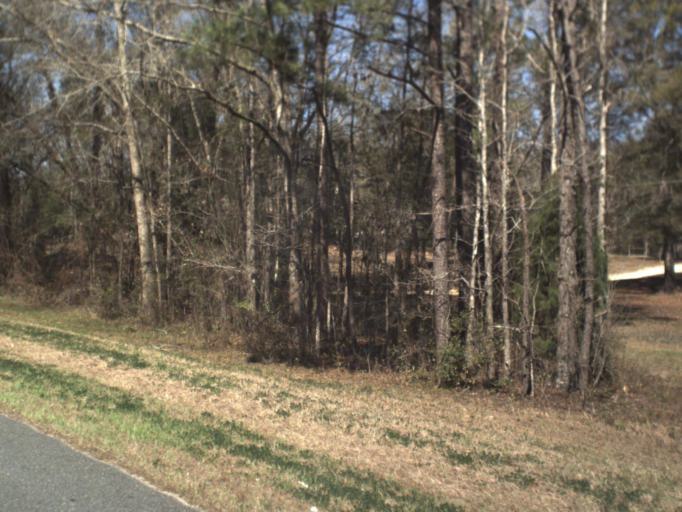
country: US
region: Florida
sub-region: Jackson County
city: Marianna
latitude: 30.7398
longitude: -85.1210
